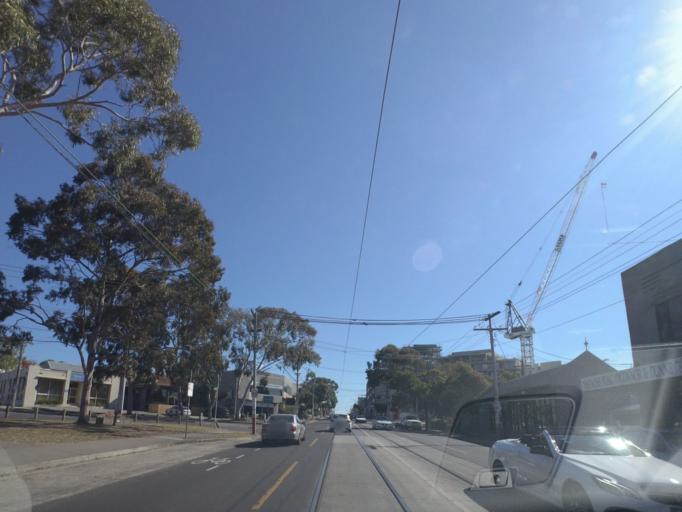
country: AU
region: Victoria
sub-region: Boroondara
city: Kew
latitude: -37.8036
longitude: 145.0398
